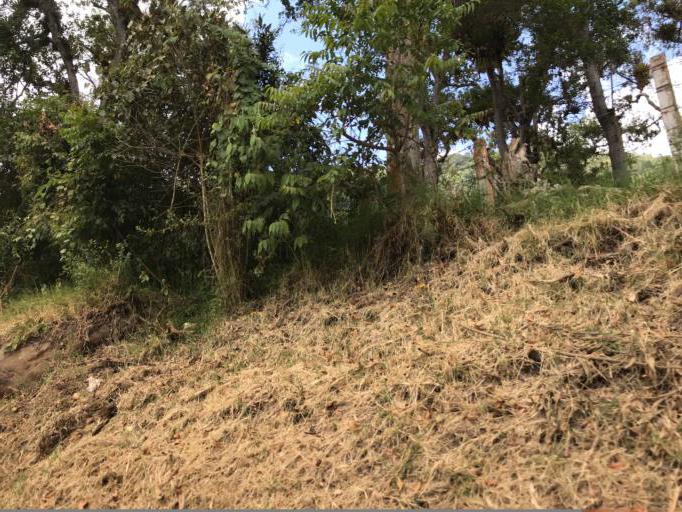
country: CO
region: Valle del Cauca
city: Cali
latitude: 3.4649
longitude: -76.6353
